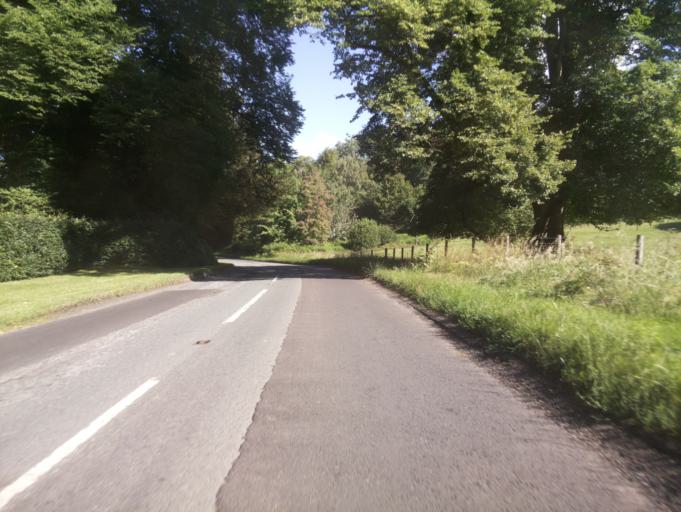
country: GB
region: England
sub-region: Herefordshire
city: Yatton
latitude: 51.9621
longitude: -2.5446
